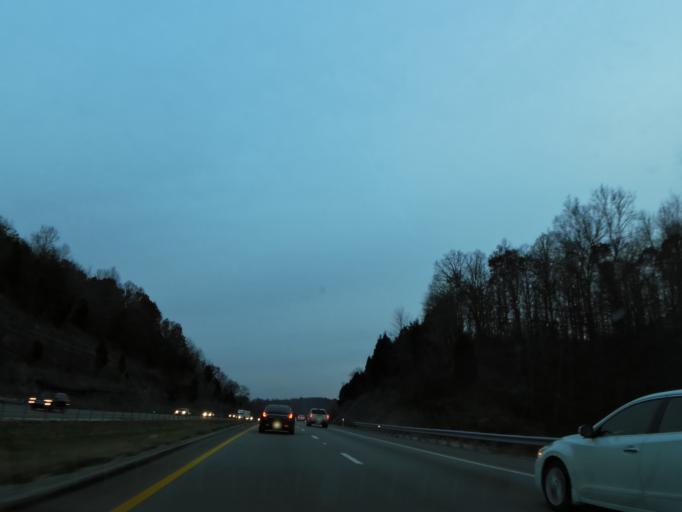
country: US
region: Kentucky
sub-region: Rockcastle County
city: Brodhead
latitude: 37.4525
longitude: -84.3359
